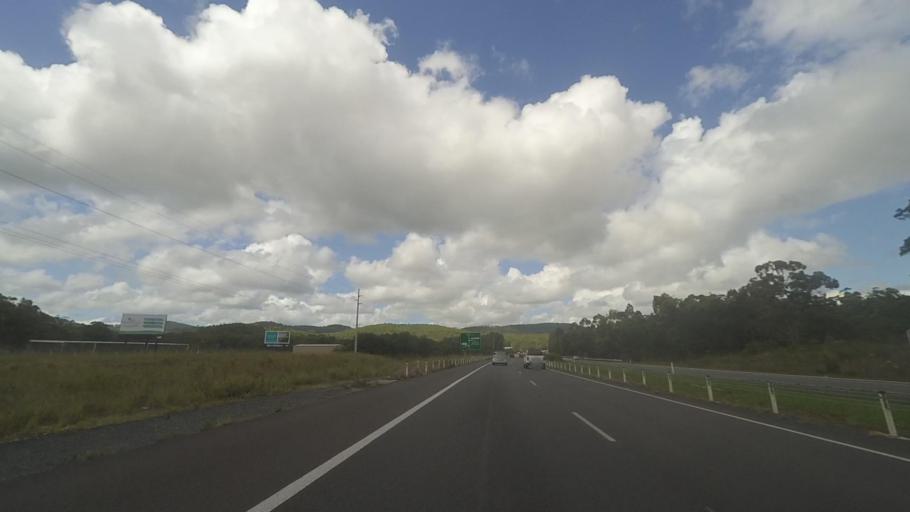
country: AU
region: New South Wales
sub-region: Great Lakes
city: Bulahdelah
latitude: -32.3896
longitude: 152.2232
